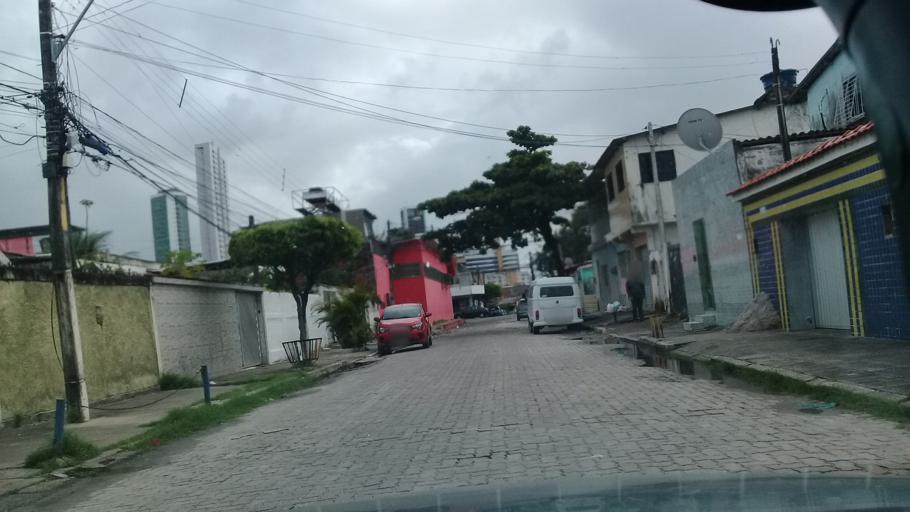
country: BR
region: Pernambuco
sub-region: Recife
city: Recife
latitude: -8.0358
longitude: -34.8794
